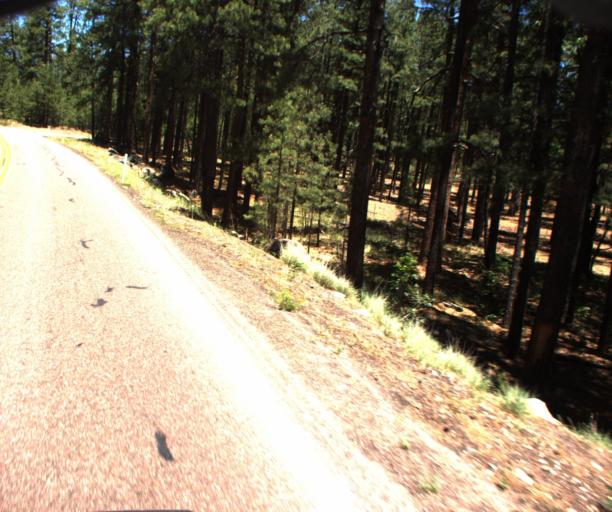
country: US
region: Arizona
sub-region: Gila County
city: Pine
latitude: 34.5122
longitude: -111.3407
